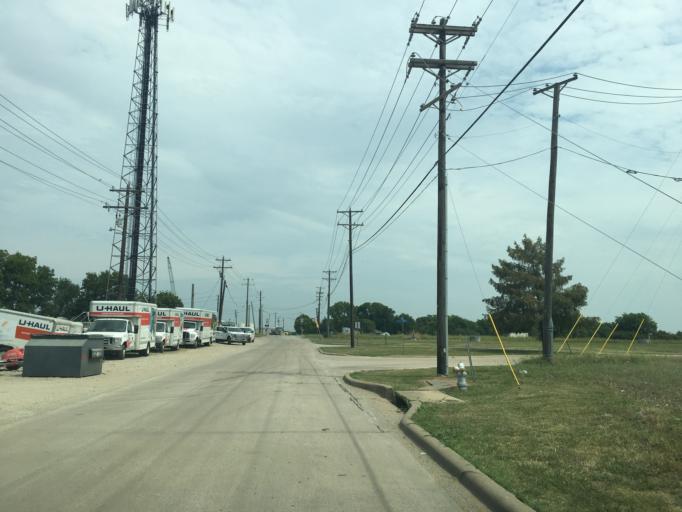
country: US
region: Texas
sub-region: Collin County
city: Wylie
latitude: 33.0238
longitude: -96.5194
